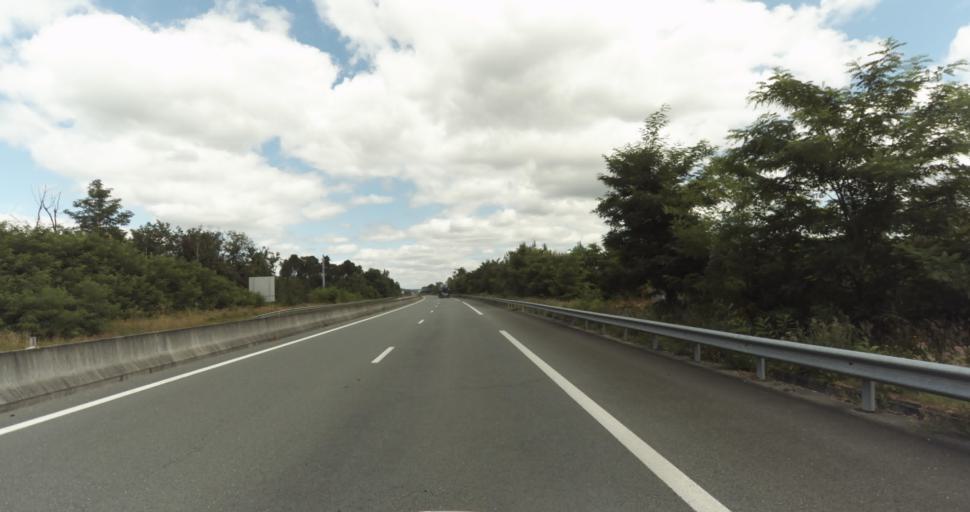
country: FR
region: Aquitaine
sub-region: Departement de la Gironde
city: Bazas
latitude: 44.4592
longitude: -0.2256
